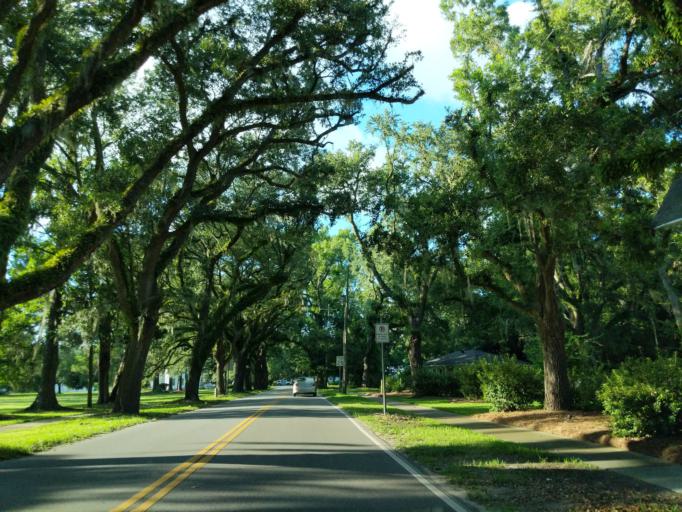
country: US
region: South Carolina
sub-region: Charleston County
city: Awendaw
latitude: 33.0861
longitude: -79.4608
